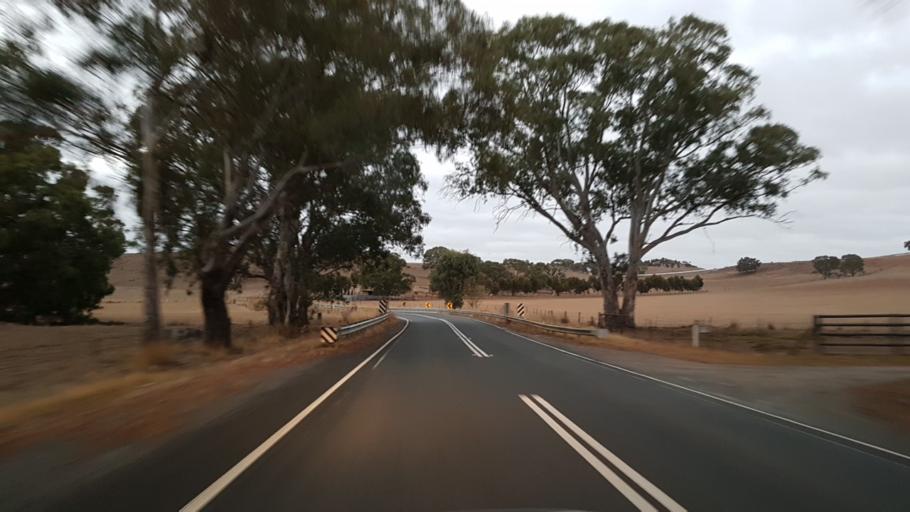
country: AU
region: South Australia
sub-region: Mount Barker
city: Nairne
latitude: -35.0403
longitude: 138.9871
